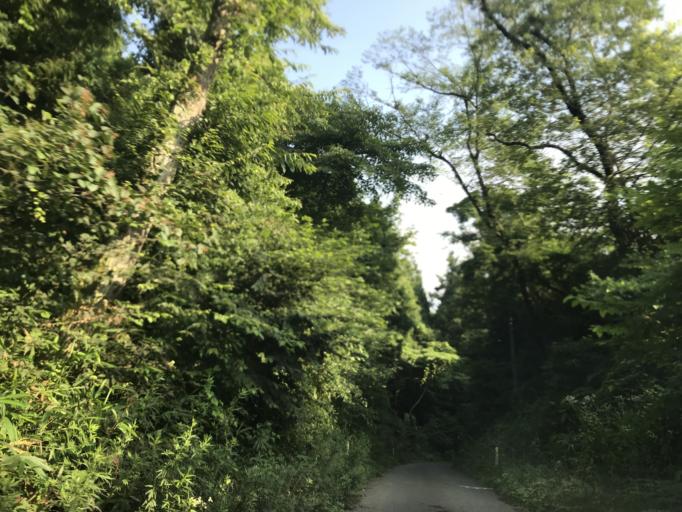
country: JP
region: Iwate
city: Ichinoseki
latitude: 38.8512
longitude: 141.1153
